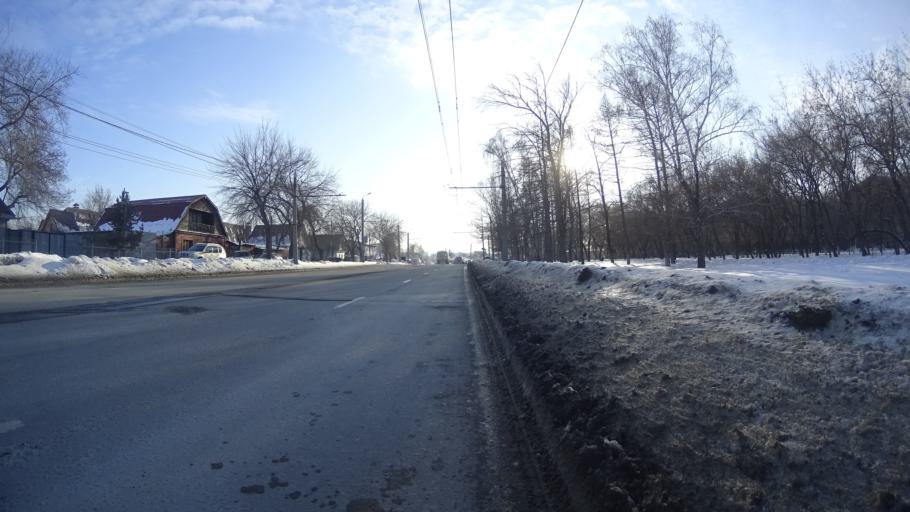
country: RU
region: Chelyabinsk
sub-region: Gorod Chelyabinsk
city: Chelyabinsk
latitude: 55.1853
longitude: 61.4596
